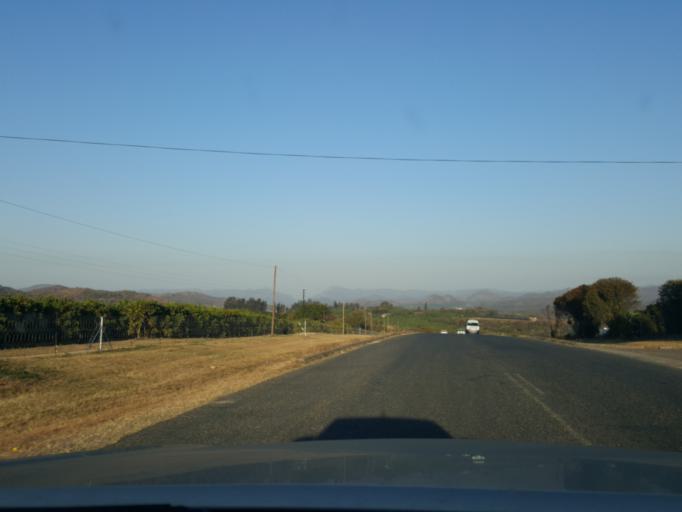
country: ZA
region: Mpumalanga
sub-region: Ehlanzeni District
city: Nelspruit
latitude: -25.4375
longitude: 30.9943
